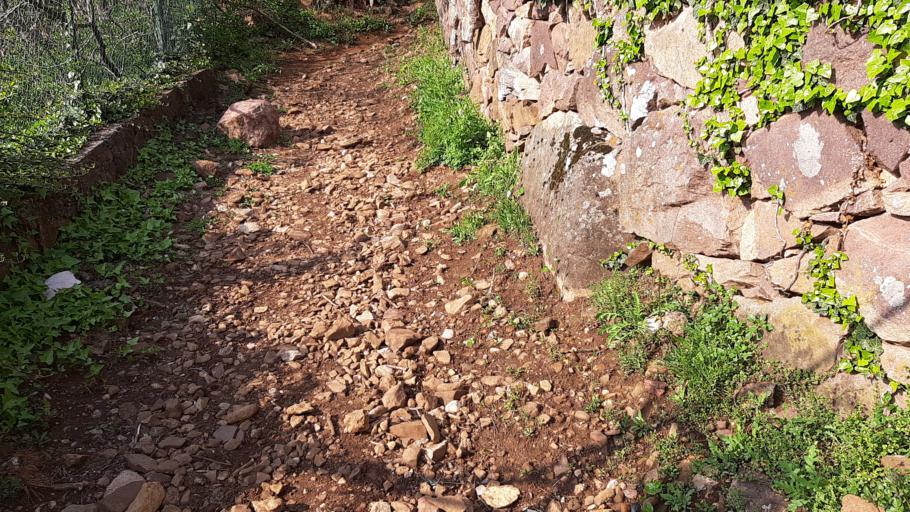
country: IT
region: Trentino-Alto Adige
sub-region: Provincia di Trento
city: Lavis
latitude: 46.1459
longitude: 11.1133
